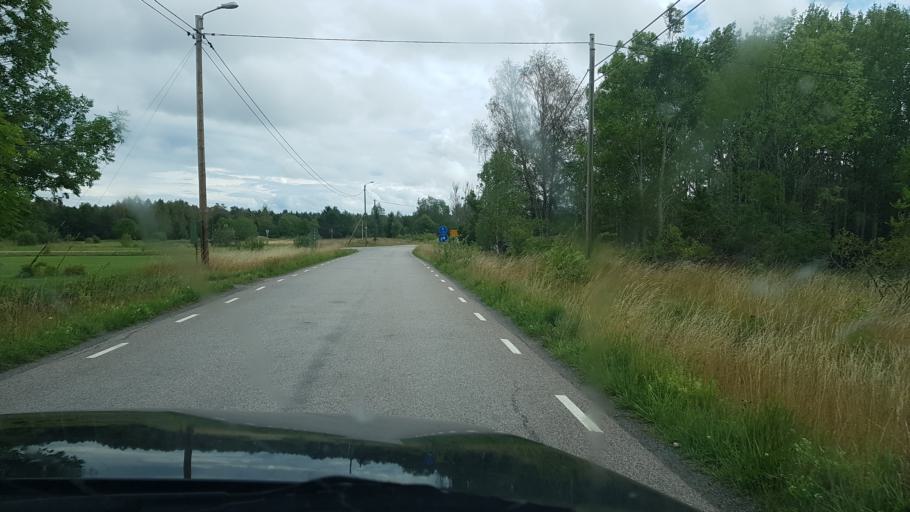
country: SE
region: Uppsala
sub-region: Osthammars Kommun
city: Oregrund
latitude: 60.3562
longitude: 18.4517
